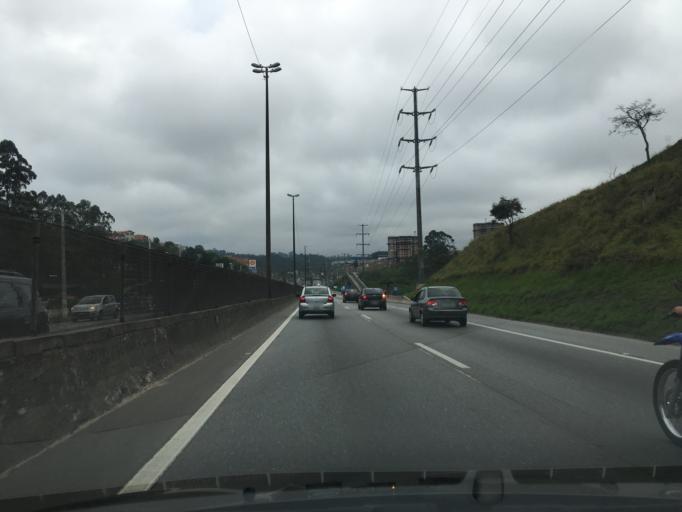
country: BR
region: Sao Paulo
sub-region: Taboao Da Serra
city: Taboao da Serra
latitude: -23.6322
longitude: -46.8222
